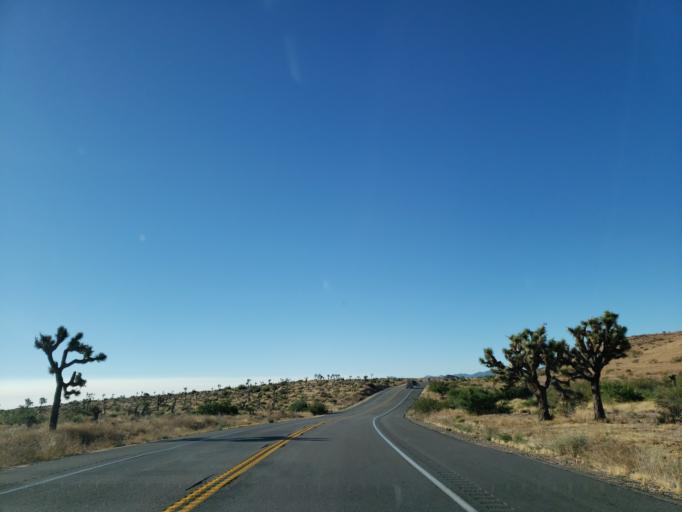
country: US
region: California
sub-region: San Bernardino County
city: Yucca Valley
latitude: 34.1876
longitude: -116.4330
